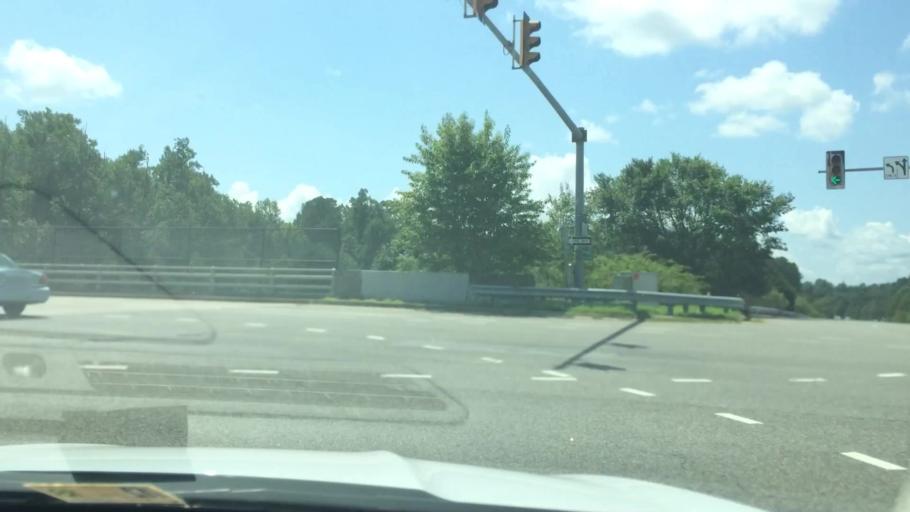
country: US
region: Virginia
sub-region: James City County
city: Williamsburg
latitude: 37.2995
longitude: -76.7460
